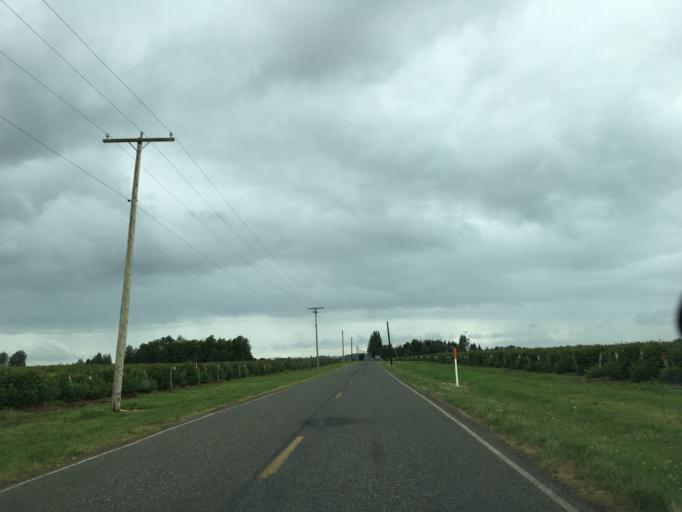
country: US
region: Washington
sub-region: Whatcom County
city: Lynden
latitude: 48.9787
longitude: -122.4099
